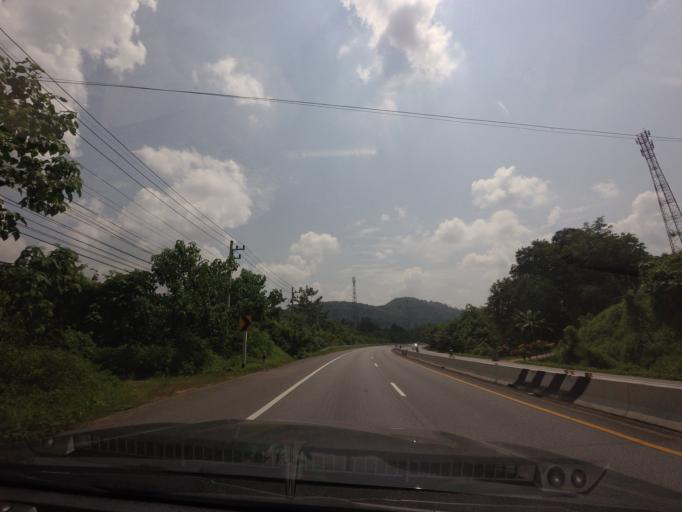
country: TH
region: Uttaradit
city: Lap Lae
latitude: 17.8023
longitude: 100.1139
